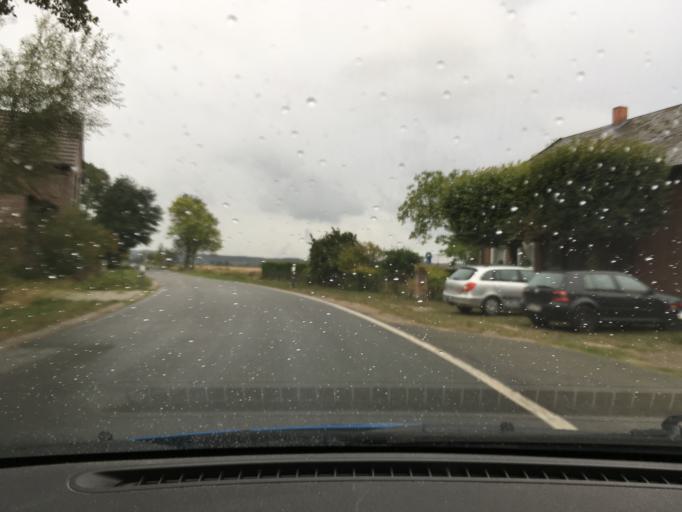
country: DE
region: Lower Saxony
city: Hitzacker
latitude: 53.1930
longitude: 11.0381
